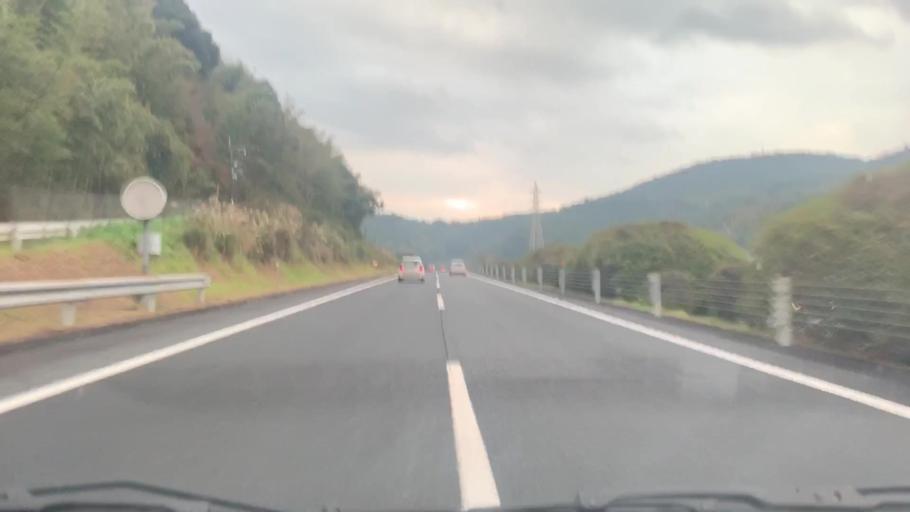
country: JP
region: Nagasaki
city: Omura
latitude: 32.8819
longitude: 129.9958
